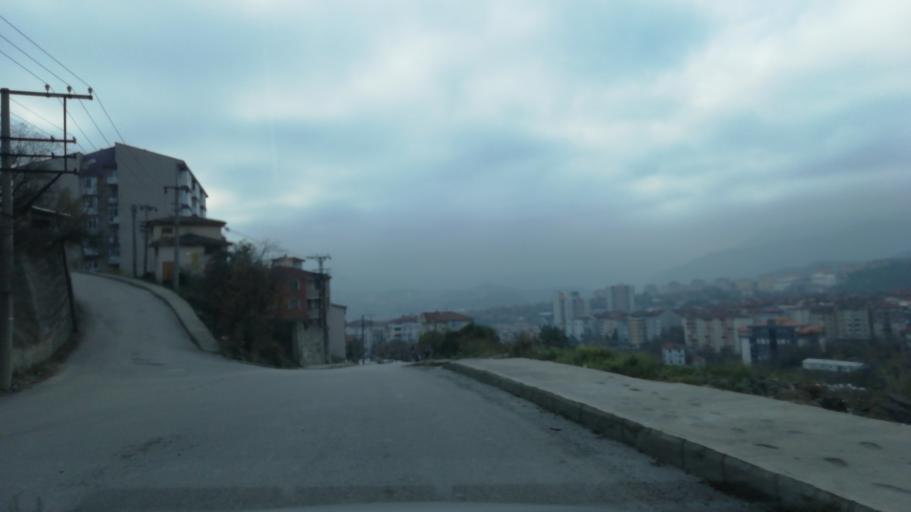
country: TR
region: Karabuk
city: Karabuk
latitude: 41.2111
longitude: 32.6284
